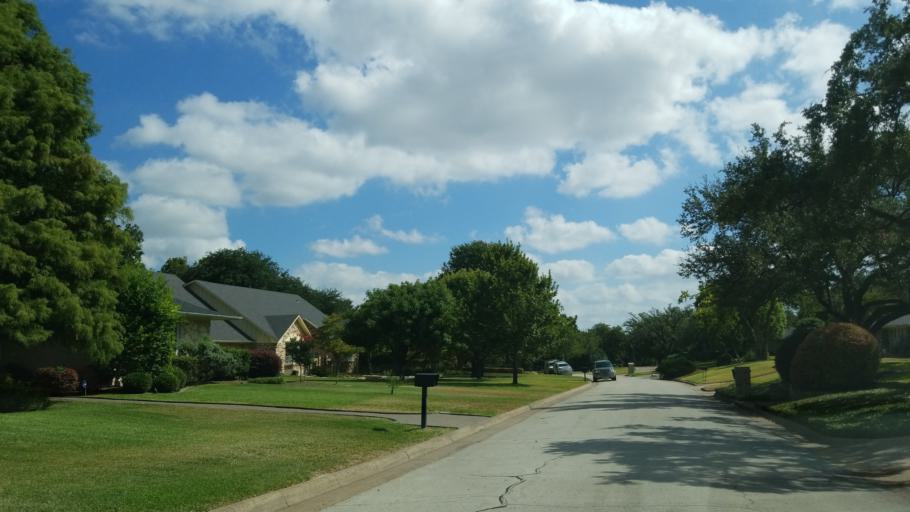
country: US
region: Texas
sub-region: Dallas County
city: Addison
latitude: 32.9311
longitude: -96.8015
